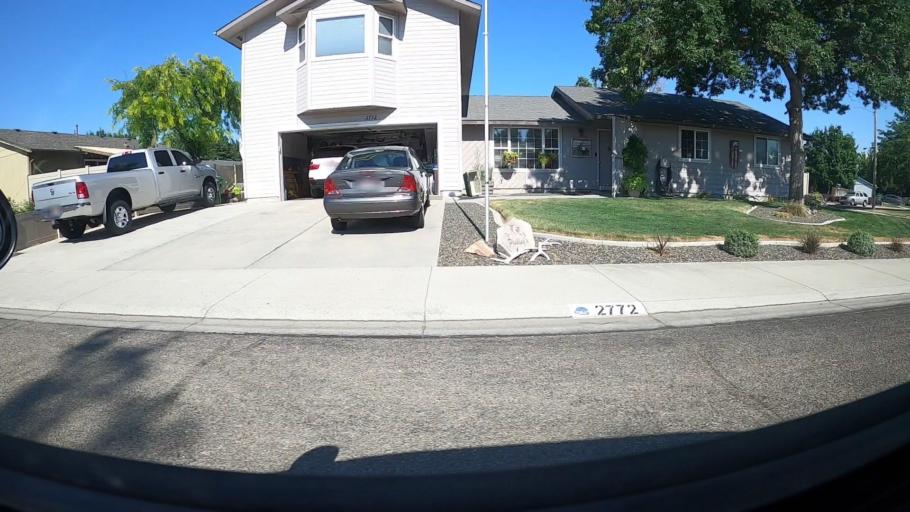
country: US
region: Idaho
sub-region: Ada County
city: Meridian
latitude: 43.6300
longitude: -116.4128
